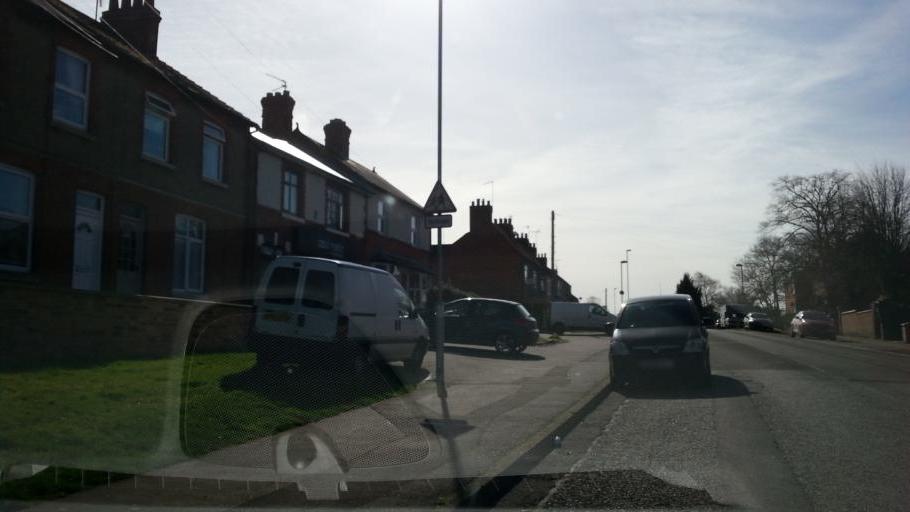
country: GB
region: England
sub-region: Northamptonshire
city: Brixworth
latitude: 52.3270
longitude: -0.9041
